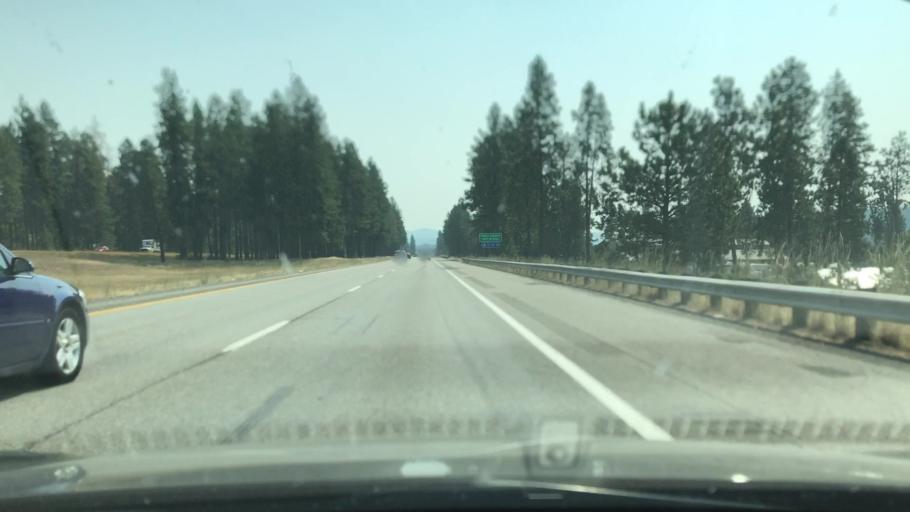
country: US
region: Idaho
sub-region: Kootenai County
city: Coeur d'Alene
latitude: 47.7070
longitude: -116.8495
